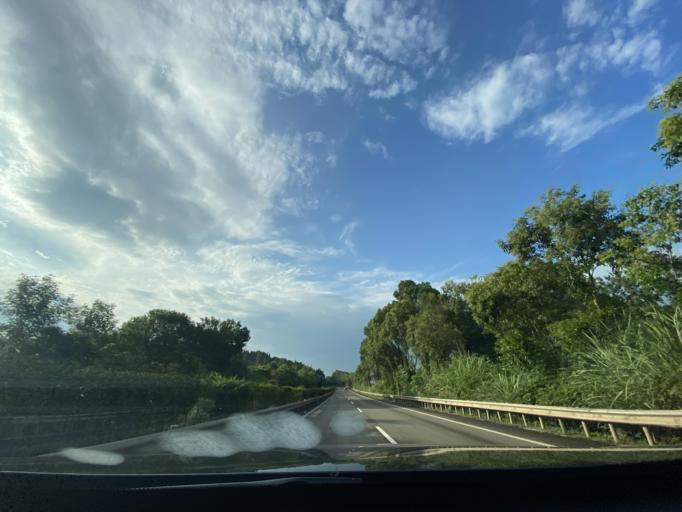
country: CN
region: Sichuan
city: Jiancheng
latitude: 30.3780
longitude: 104.5179
